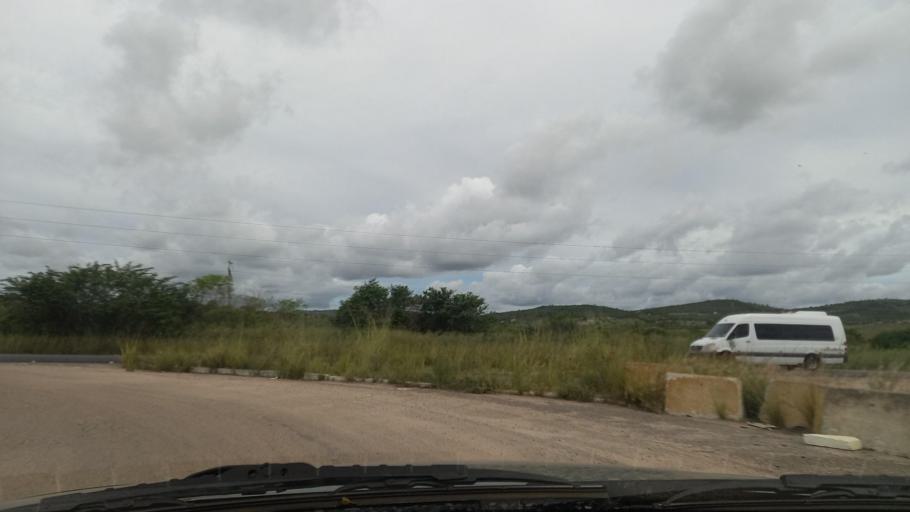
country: BR
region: Pernambuco
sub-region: Gravata
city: Gravata
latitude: -8.2159
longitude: -35.6278
